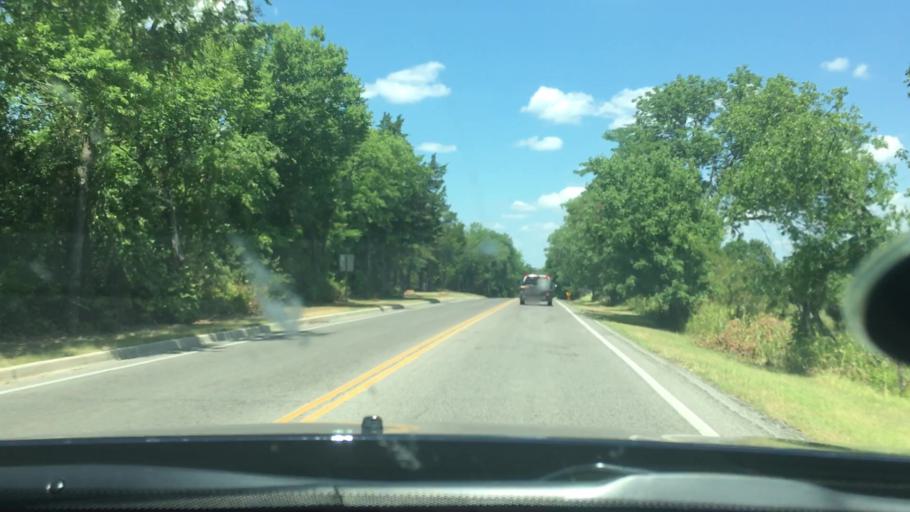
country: US
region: Oklahoma
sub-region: Murray County
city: Sulphur
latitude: 34.4964
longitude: -96.9695
